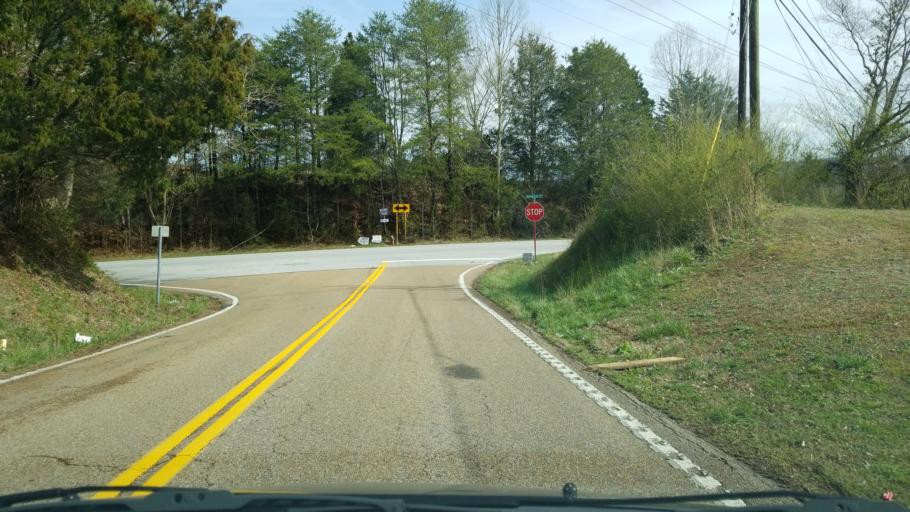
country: US
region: Tennessee
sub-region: Hamilton County
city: Lakesite
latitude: 35.1790
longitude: -85.0501
